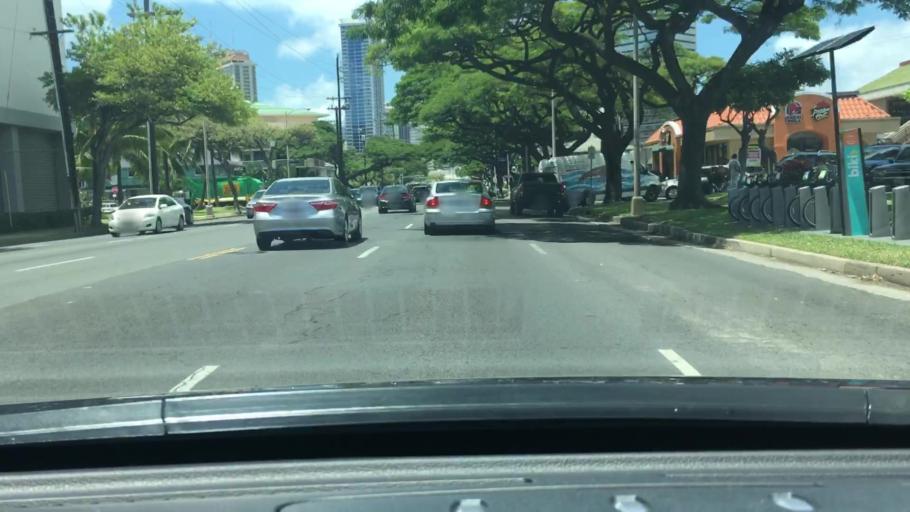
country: US
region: Hawaii
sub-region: Honolulu County
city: Honolulu
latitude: 21.2896
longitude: -157.8326
